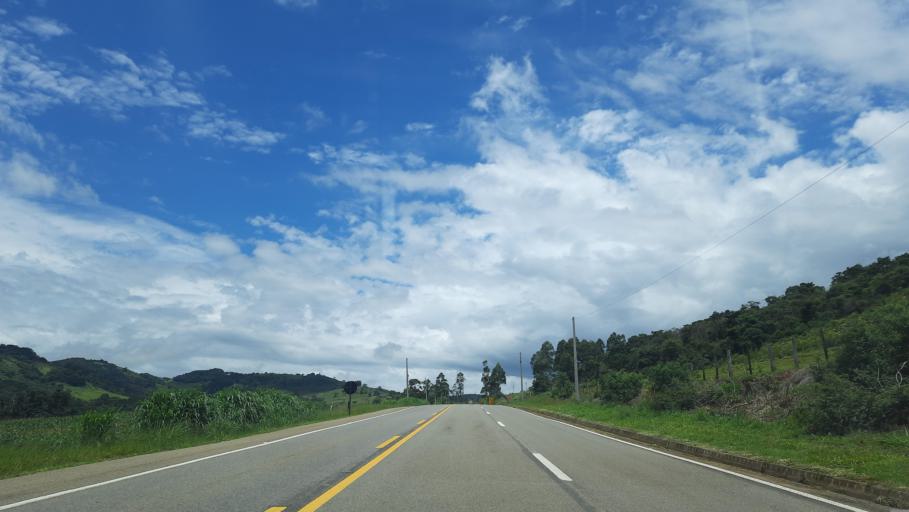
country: BR
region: Sao Paulo
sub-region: Vargem Grande Do Sul
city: Vargem Grande do Sul
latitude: -21.8284
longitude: -46.7707
